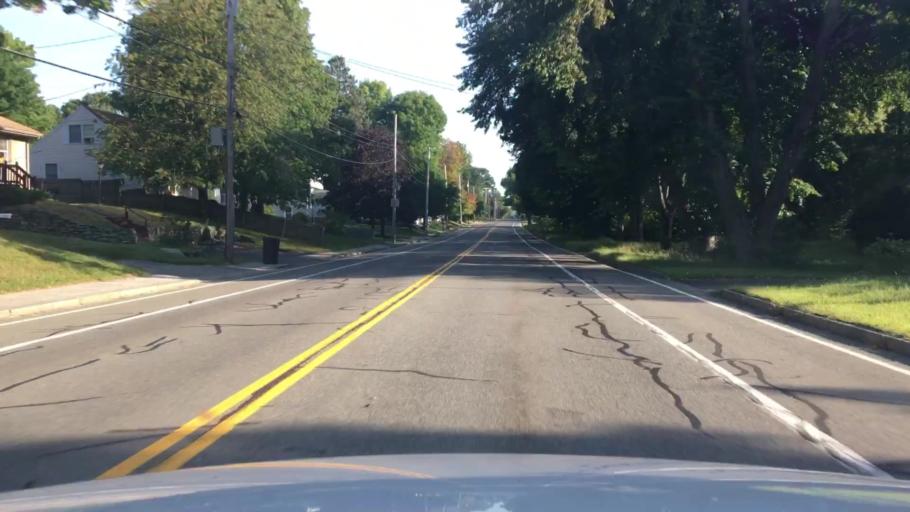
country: US
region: Maine
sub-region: Cumberland County
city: Falmouth
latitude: 43.7180
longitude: -70.2930
